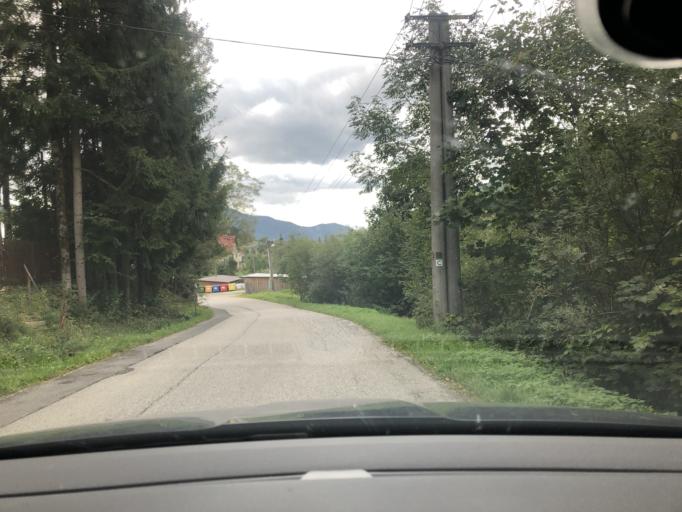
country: SK
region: Zilinsky
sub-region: Okres Zilina
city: Terchova
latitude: 49.2821
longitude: 19.0531
